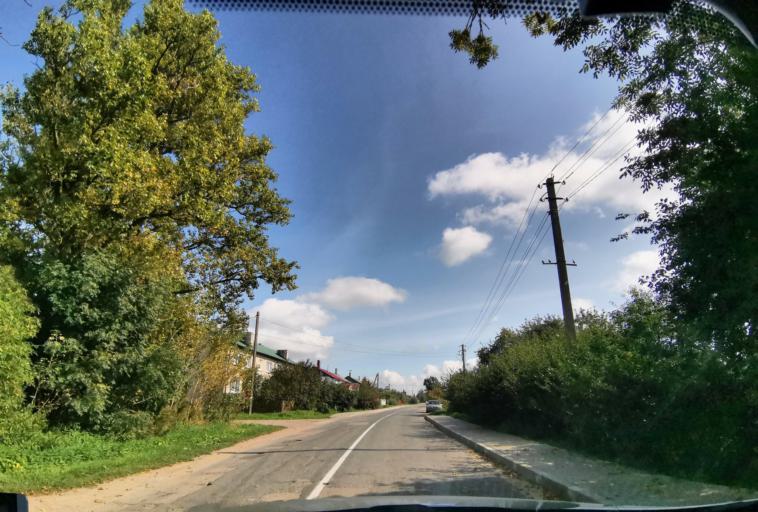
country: RU
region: Kaliningrad
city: Chernyakhovsk
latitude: 54.6519
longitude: 21.7274
